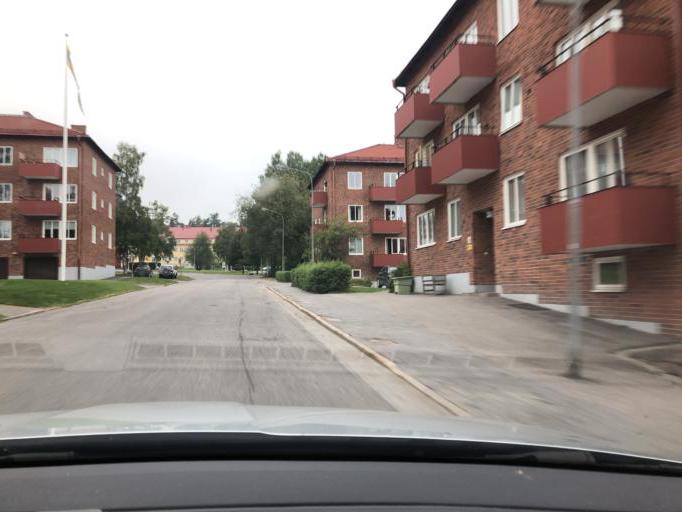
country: SE
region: Vaesternorrland
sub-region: Sundsvalls Kommun
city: Sundsvall
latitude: 62.4003
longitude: 17.3187
